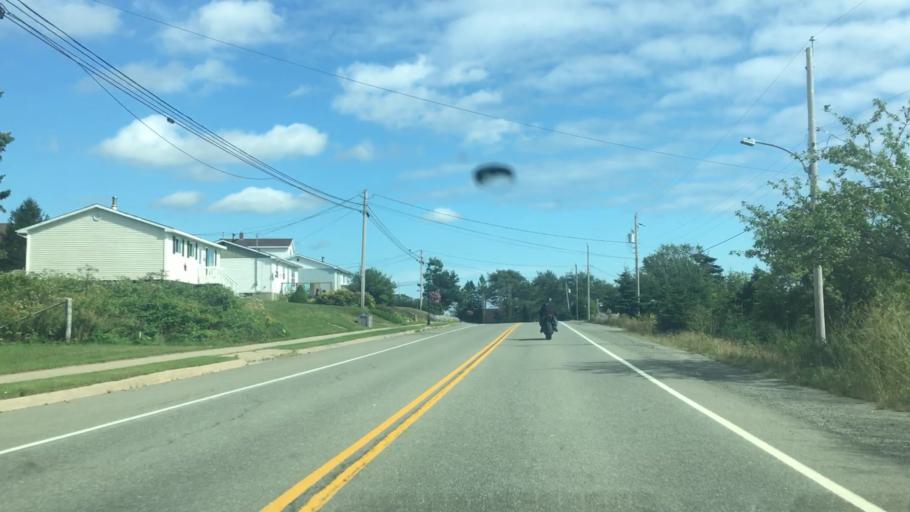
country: CA
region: Nova Scotia
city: Princeville
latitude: 45.6550
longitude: -60.8941
